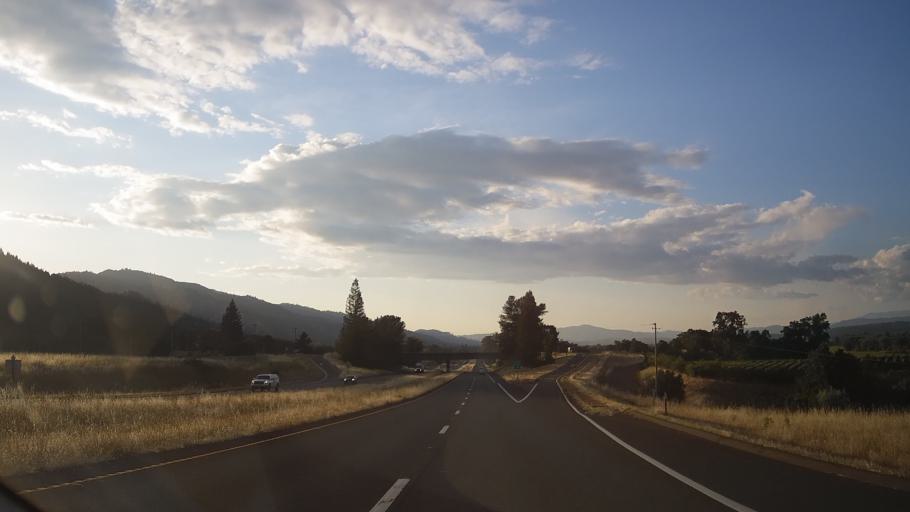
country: US
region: California
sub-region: Mendocino County
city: Talmage
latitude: 39.0813
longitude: -123.1806
